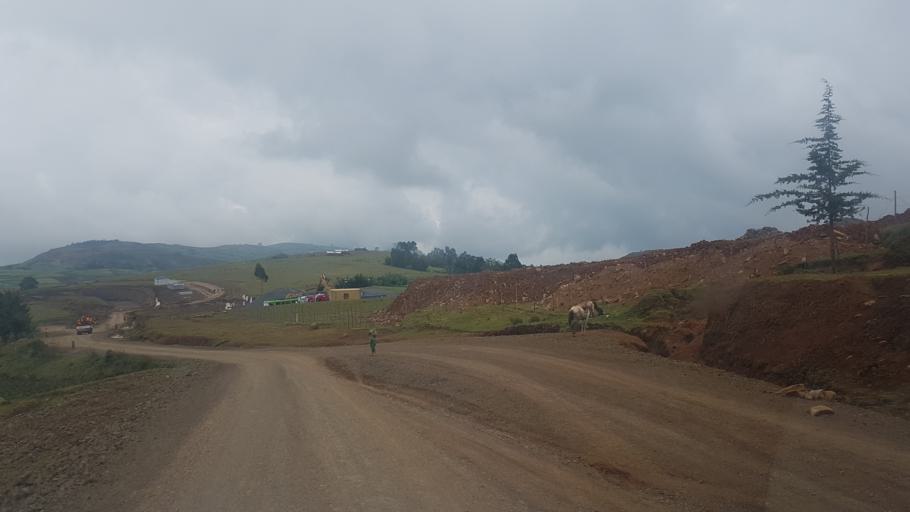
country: ET
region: Southern Nations, Nationalities, and People's Region
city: Arba Minch'
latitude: 6.3251
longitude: 37.5476
